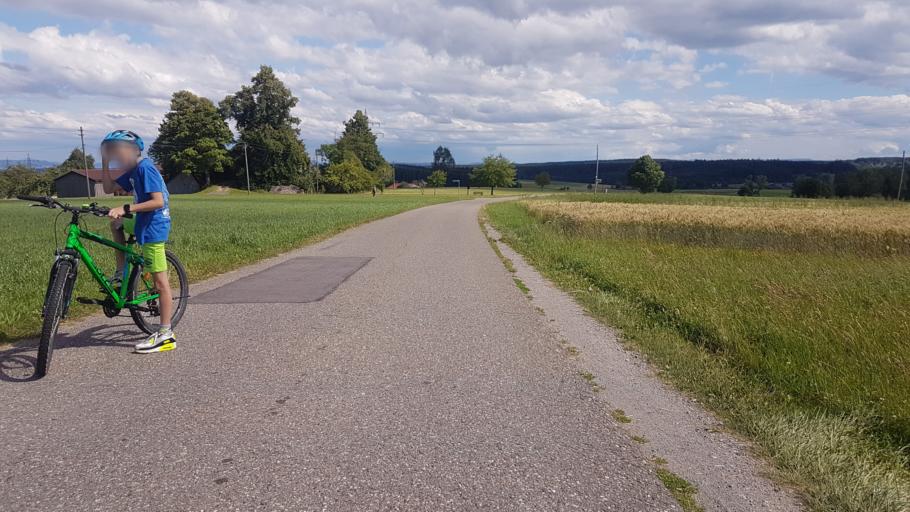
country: DE
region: Baden-Wuerttemberg
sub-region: Freiburg Region
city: Hardt
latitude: 48.1736
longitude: 8.4036
